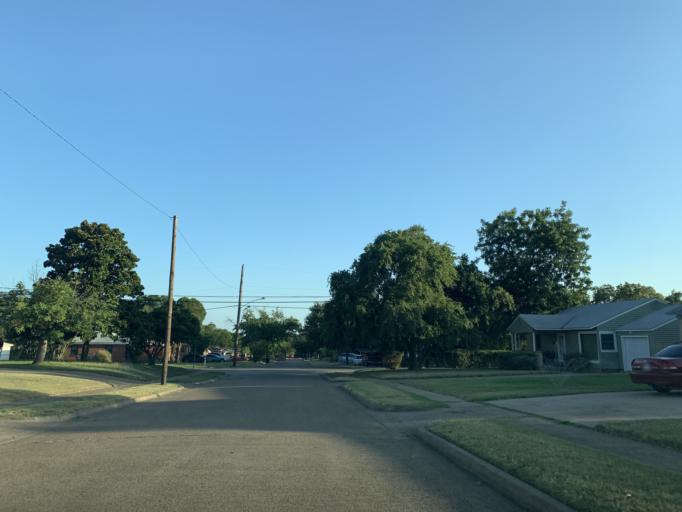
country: US
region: Texas
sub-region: Dallas County
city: Dallas
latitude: 32.6991
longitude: -96.8096
